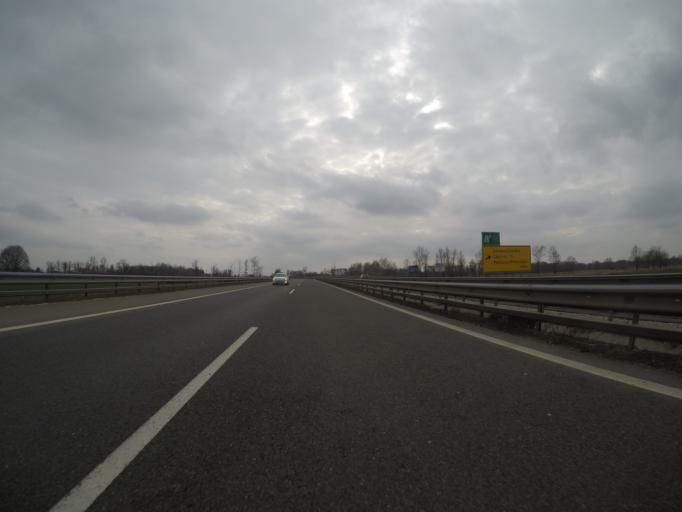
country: SI
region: Lendava-Lendva
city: Lendava
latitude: 46.5619
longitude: 16.4433
